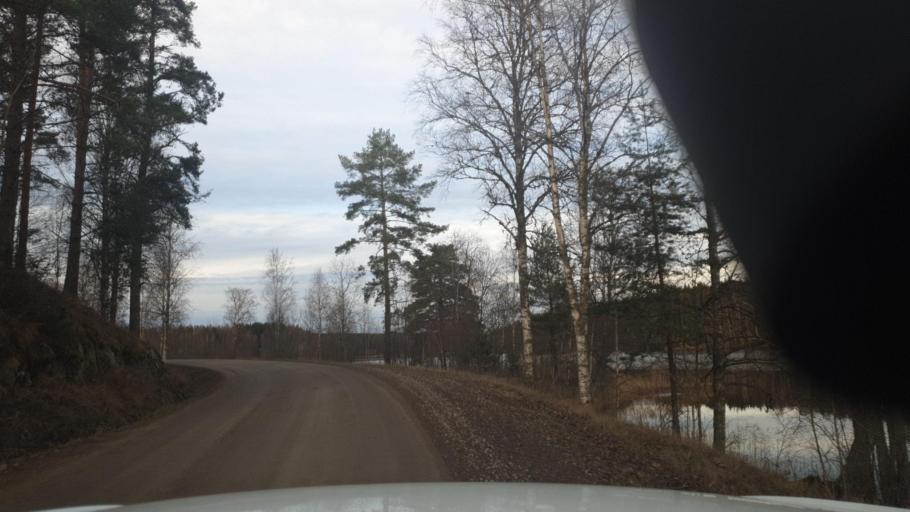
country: NO
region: Hedmark
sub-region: Eidskog
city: Skotterud
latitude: 59.8700
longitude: 11.9828
